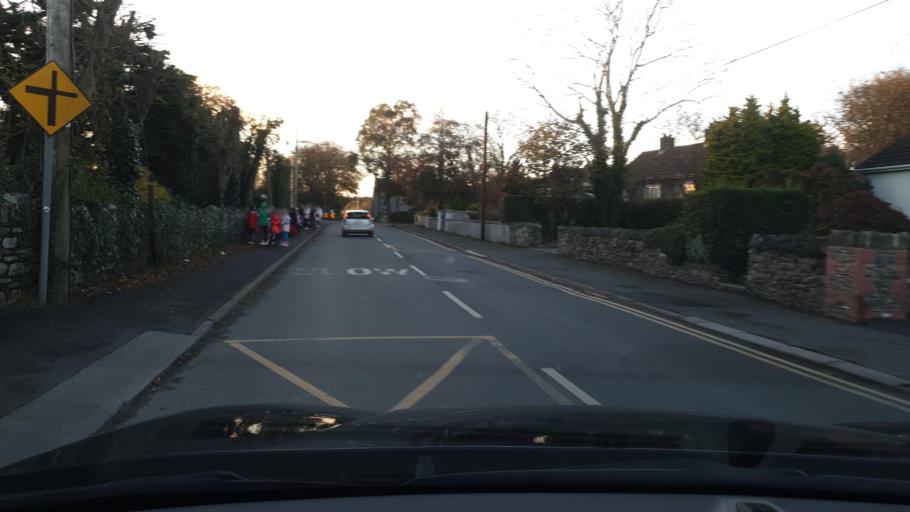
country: IE
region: Leinster
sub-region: Lu
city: Termonfeckin
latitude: 53.7623
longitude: -6.2700
